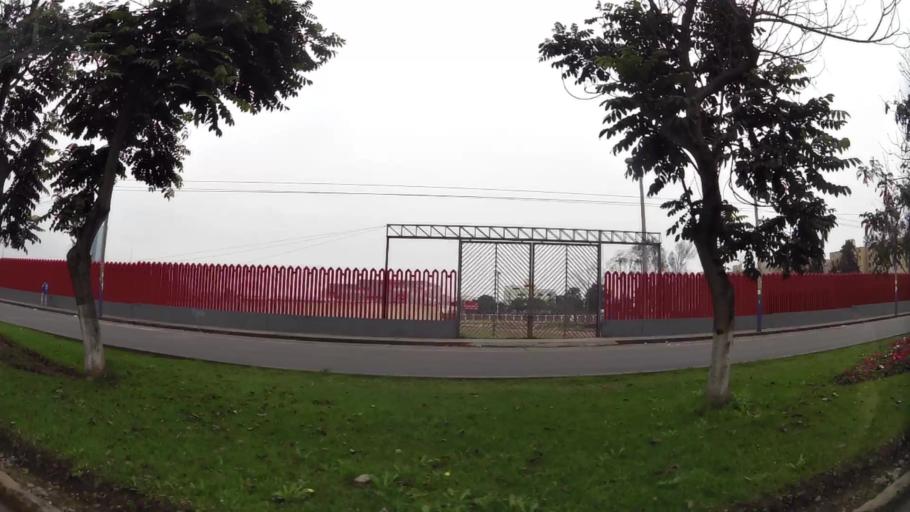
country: PE
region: Lima
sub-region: Lima
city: San Luis
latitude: -12.0791
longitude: -76.9988
